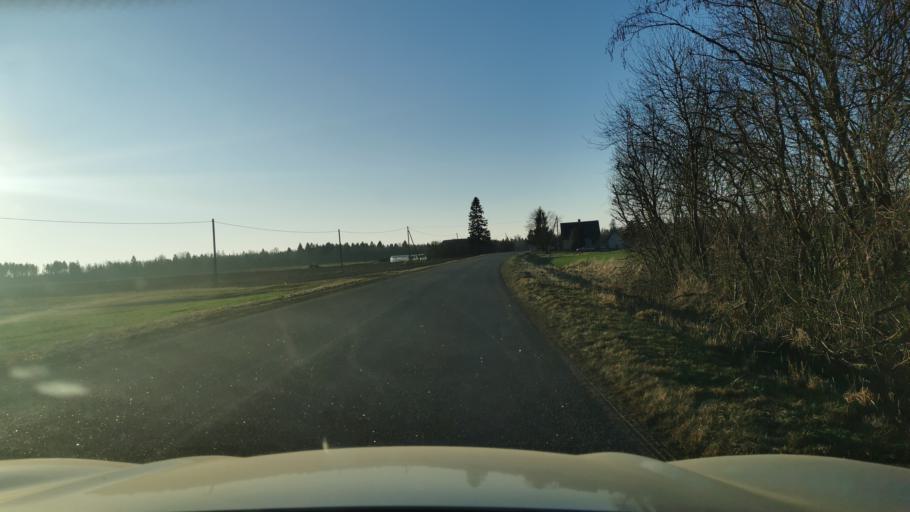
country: EE
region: Ida-Virumaa
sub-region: Kivioli linn
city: Kivioli
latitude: 59.3056
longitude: 26.9977
